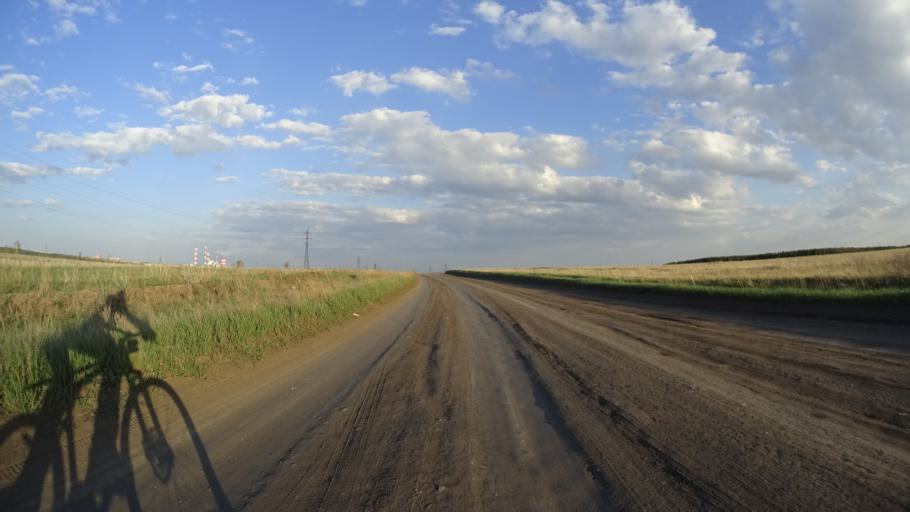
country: RU
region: Chelyabinsk
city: Troitsk
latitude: 54.0519
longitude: 61.5922
